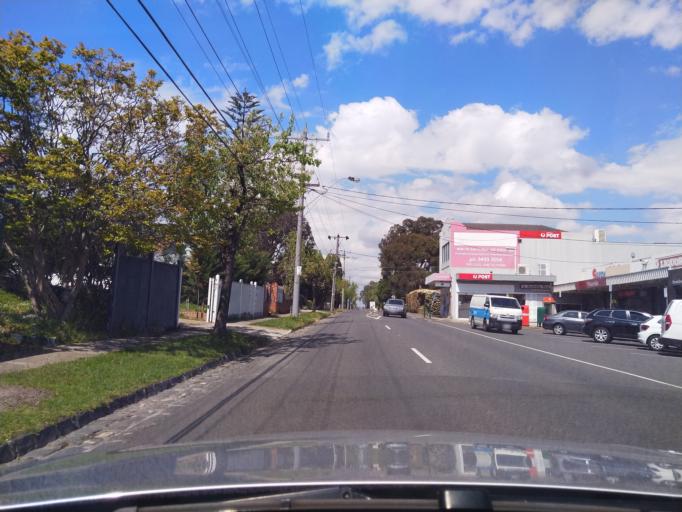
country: AU
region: Victoria
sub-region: Banyule
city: Bellfield
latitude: -37.7592
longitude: 145.0446
